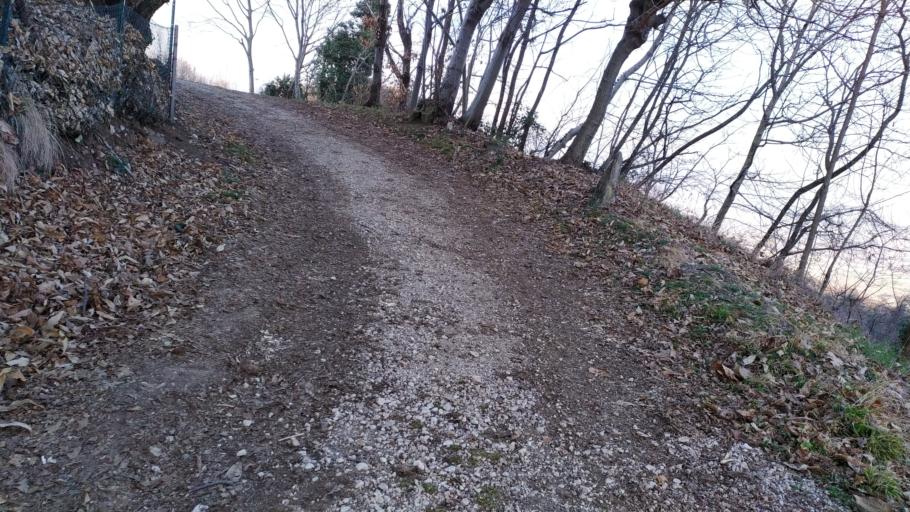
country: IT
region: Veneto
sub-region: Provincia di Vicenza
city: Monte di Malo
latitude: 45.6661
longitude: 11.3508
